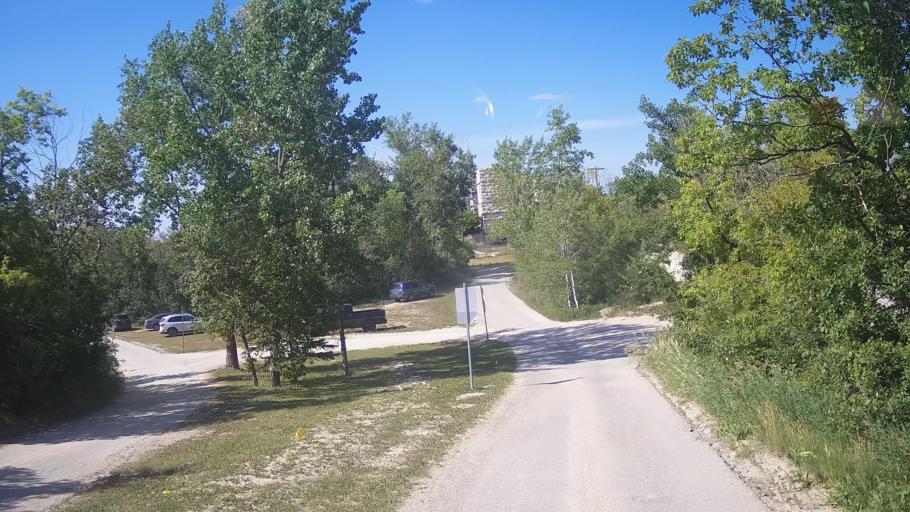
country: CA
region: Manitoba
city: Stonewall
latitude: 50.1408
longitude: -97.3267
